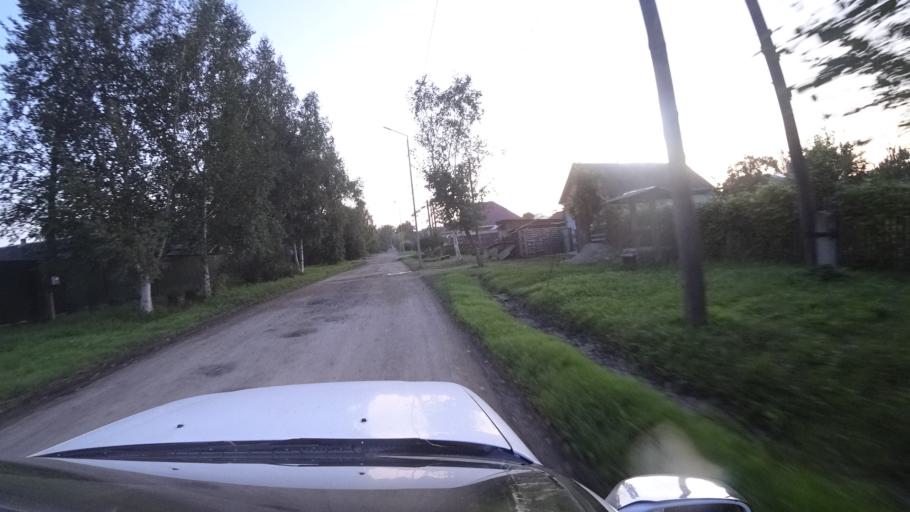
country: RU
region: Primorskiy
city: Dal'nerechensk
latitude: 45.9319
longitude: 133.7414
